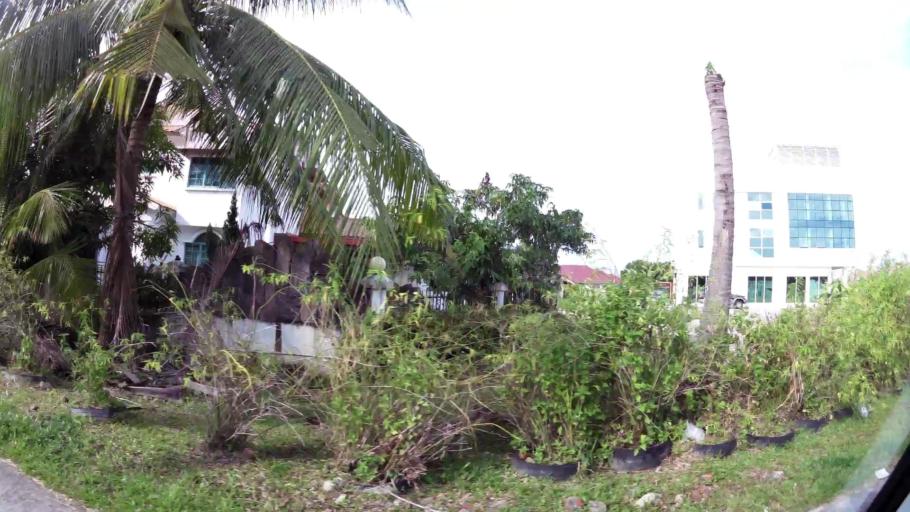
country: BN
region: Brunei and Muara
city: Bandar Seri Begawan
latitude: 4.9032
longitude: 114.8915
